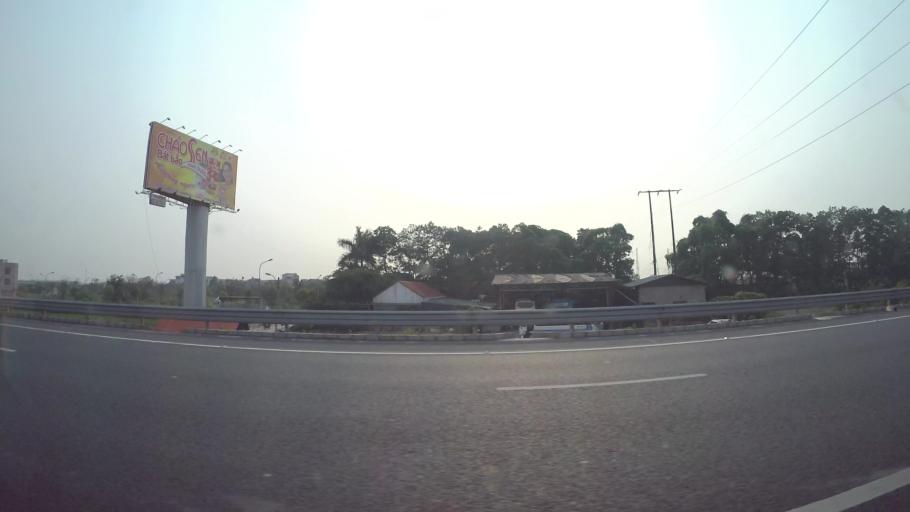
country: VN
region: Ha Noi
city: Van Dien
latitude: 20.9101
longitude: 105.8605
